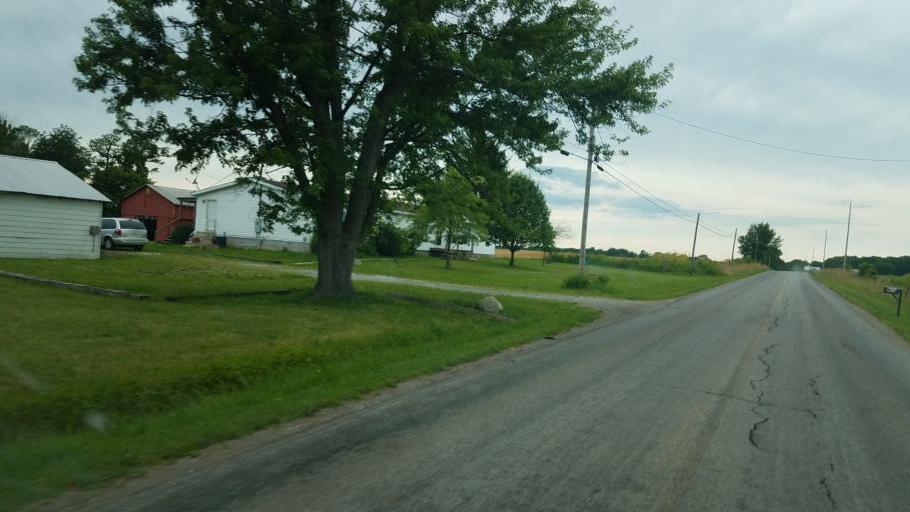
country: US
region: Ohio
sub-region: Huron County
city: Greenwich
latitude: 40.9236
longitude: -82.4441
